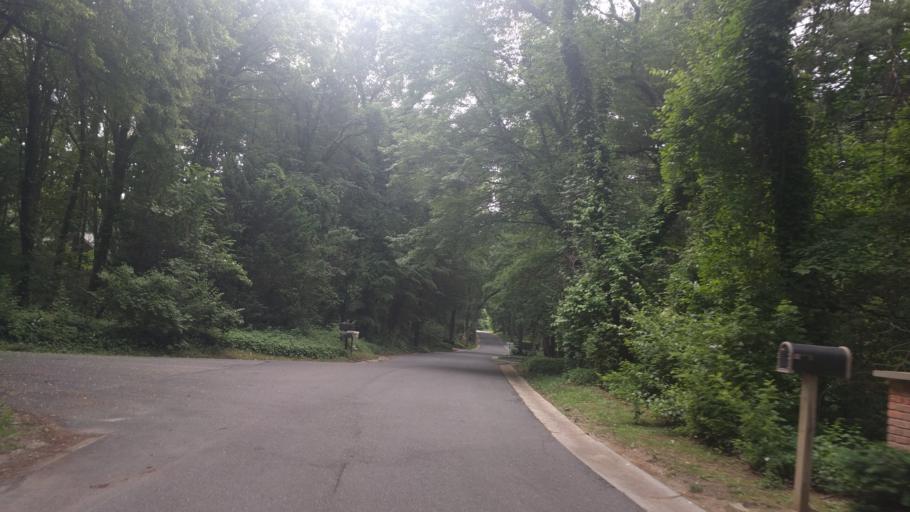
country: US
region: New York
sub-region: Nassau County
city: Old Brookville
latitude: 40.8365
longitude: -73.6053
